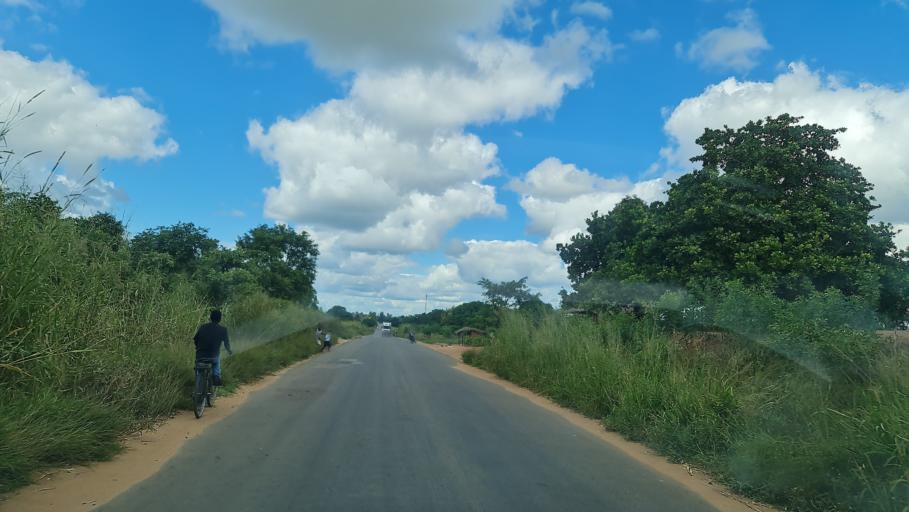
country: MZ
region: Zambezia
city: Quelimane
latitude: -17.5158
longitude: 36.2607
